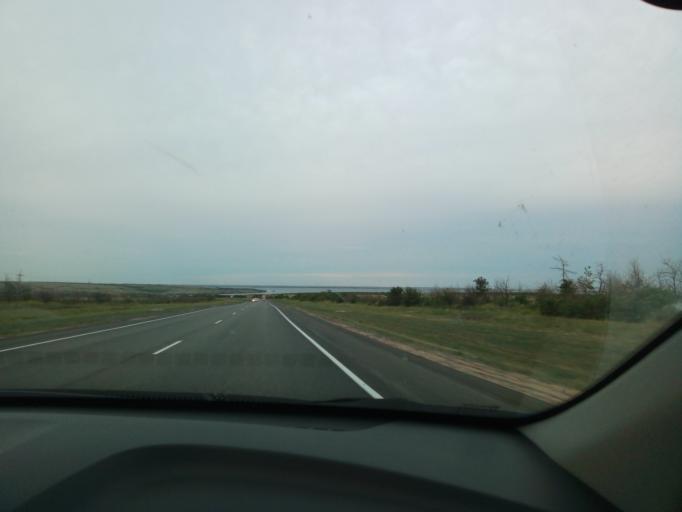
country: RU
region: Volgograd
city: Dubovka
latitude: 49.1568
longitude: 44.8475
